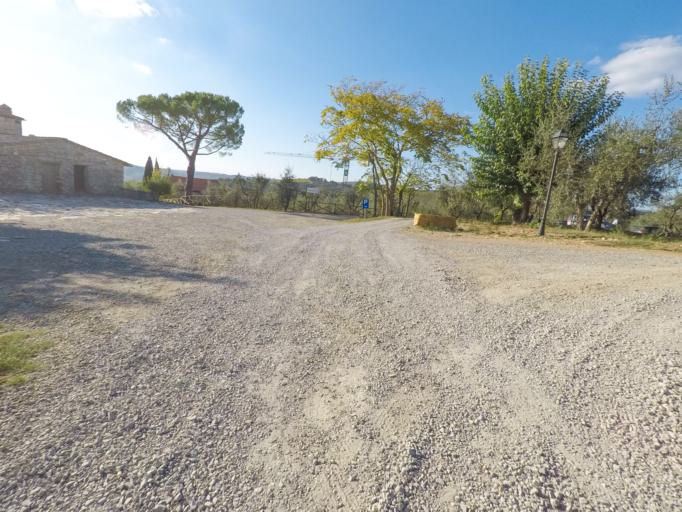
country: IT
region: Tuscany
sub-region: Provincia di Siena
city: Radda in Chianti
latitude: 43.4412
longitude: 11.3905
